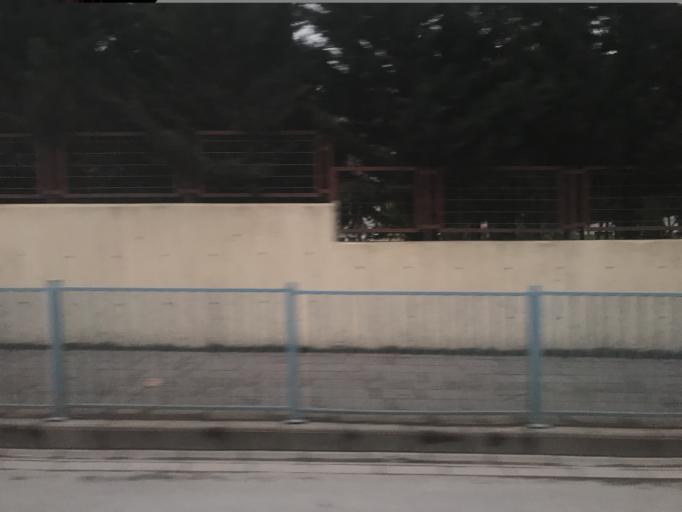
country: TR
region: Istanbul
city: Maltepe
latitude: 40.9155
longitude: 29.1703
